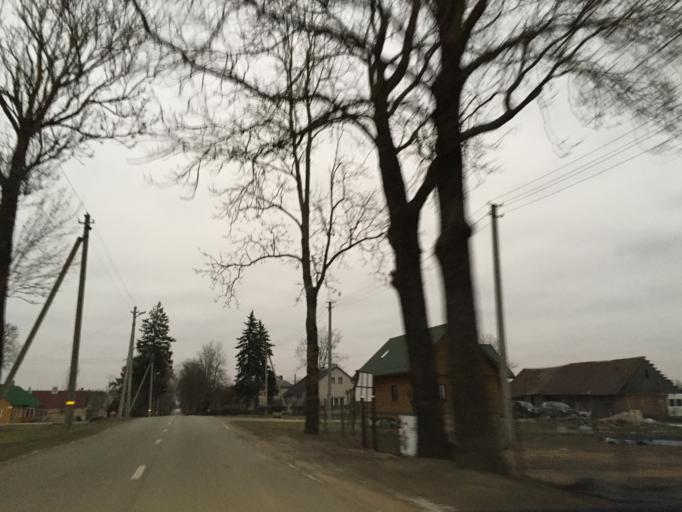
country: LT
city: Zagare
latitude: 56.3439
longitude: 23.3067
